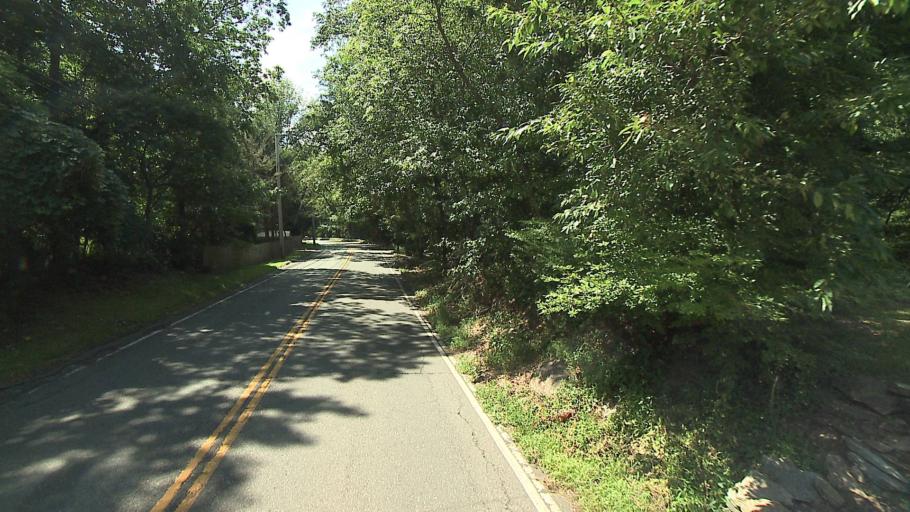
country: US
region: Connecticut
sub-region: Fairfield County
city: Shelton
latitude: 41.3012
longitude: -73.1366
